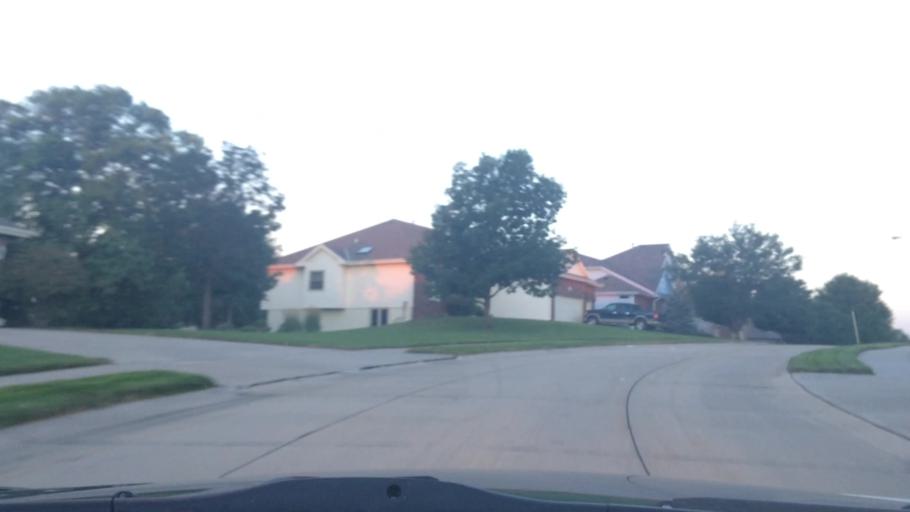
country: US
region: Nebraska
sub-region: Sarpy County
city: La Vista
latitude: 41.1822
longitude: -96.0556
